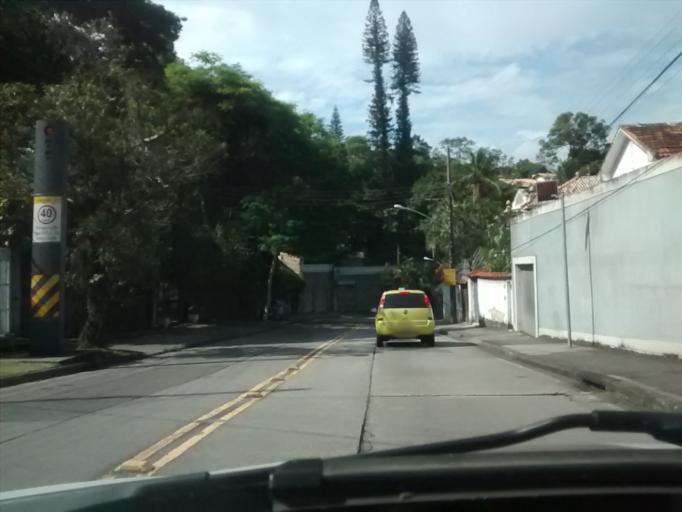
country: BR
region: Rio de Janeiro
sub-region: Rio De Janeiro
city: Rio de Janeiro
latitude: -22.9501
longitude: -43.2619
